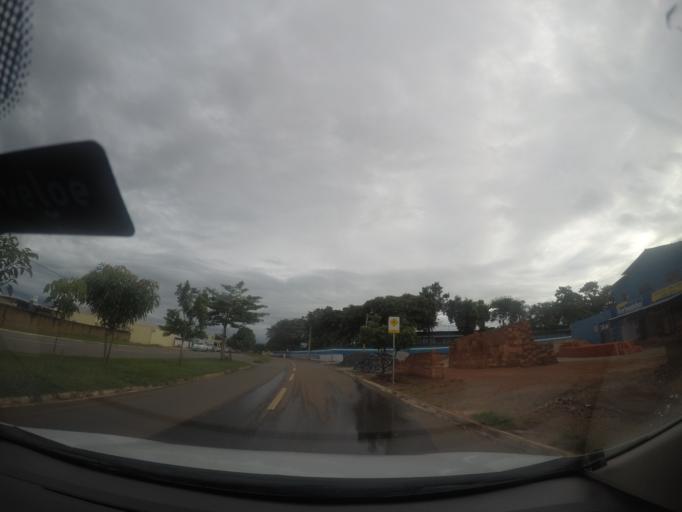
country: BR
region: Goias
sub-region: Goiania
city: Goiania
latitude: -16.6078
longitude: -49.3357
